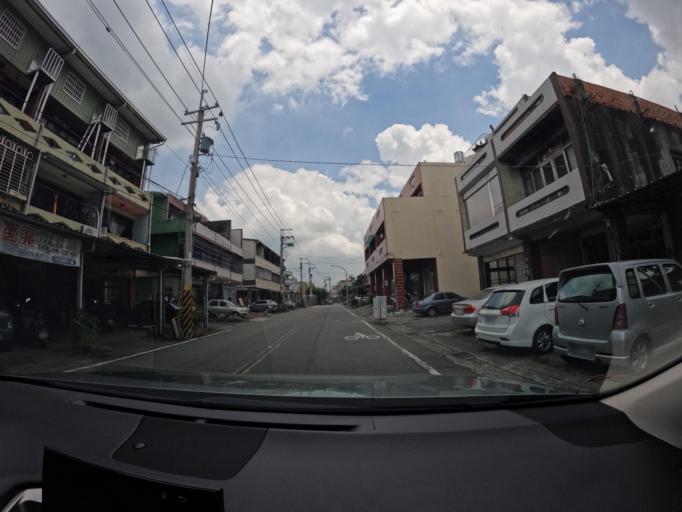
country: TW
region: Taiwan
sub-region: Nantou
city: Nantou
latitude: 23.9098
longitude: 120.6386
